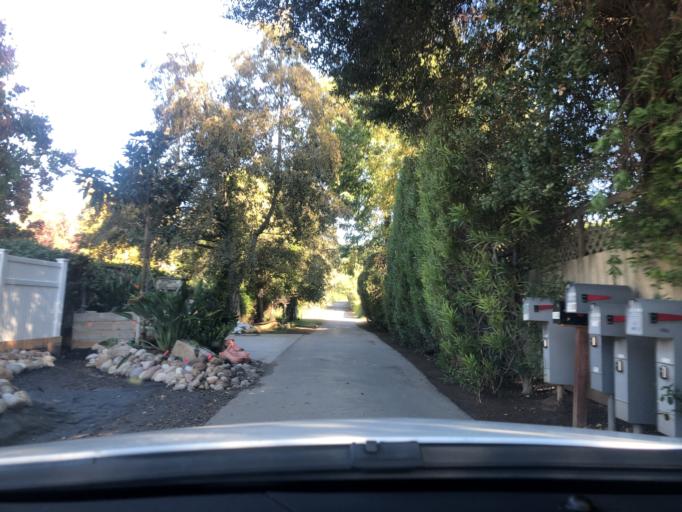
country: US
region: California
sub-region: San Diego County
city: Rancho San Diego
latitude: 32.7754
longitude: -116.9402
